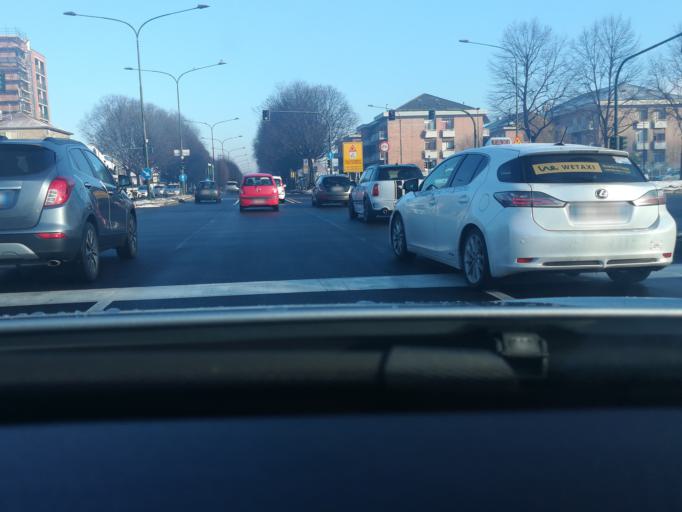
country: IT
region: Piedmont
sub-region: Provincia di Torino
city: Turin
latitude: 45.0871
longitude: 7.6515
